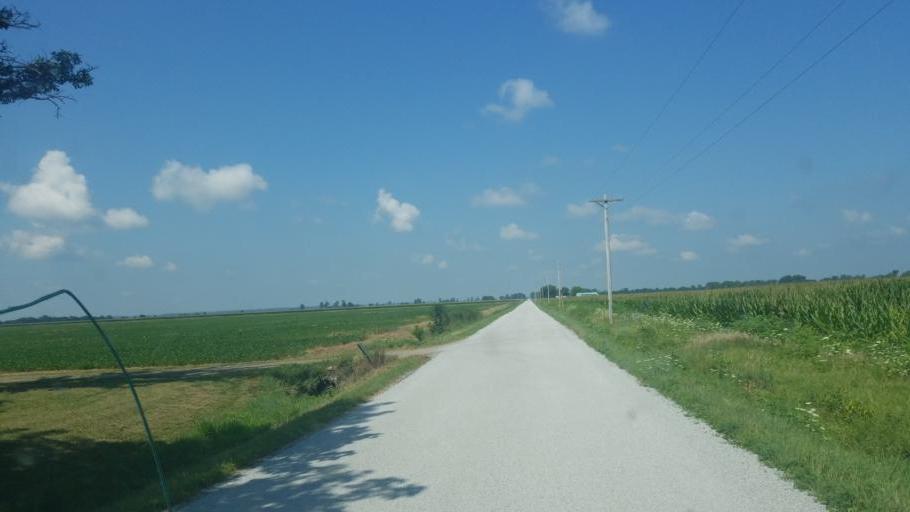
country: US
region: Ohio
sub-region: Hardin County
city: Ada
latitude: 40.6743
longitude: -83.7460
